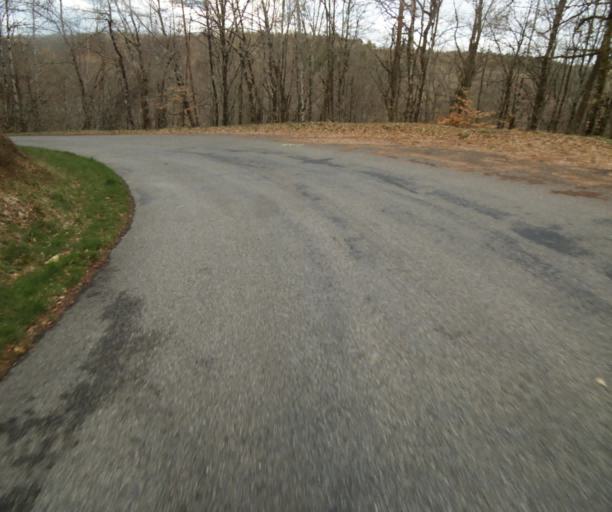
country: FR
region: Limousin
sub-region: Departement de la Correze
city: Argentat
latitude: 45.2268
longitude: 1.9853
